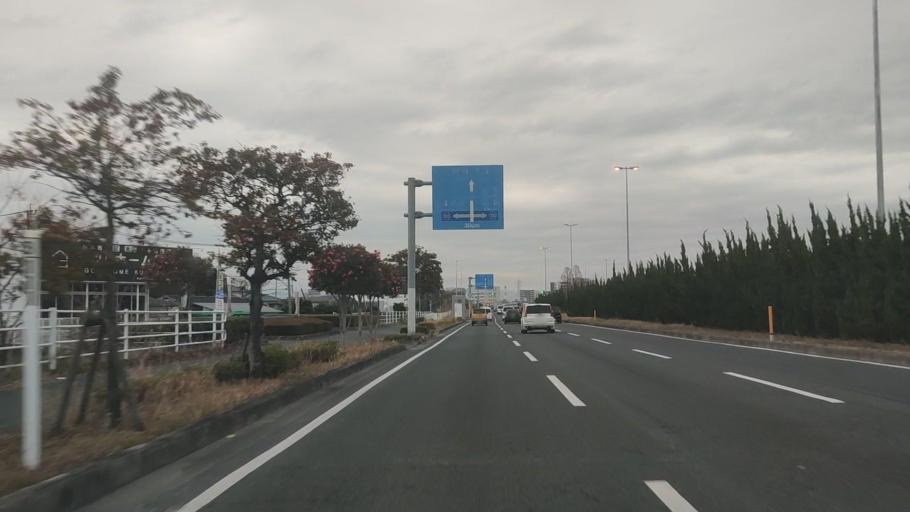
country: JP
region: Kumamoto
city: Kumamoto
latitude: 32.7751
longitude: 130.7365
